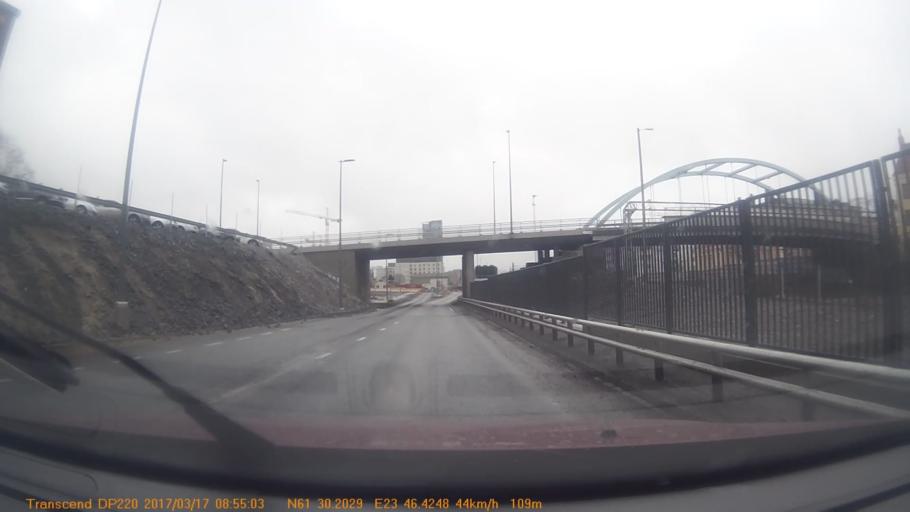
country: FI
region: Pirkanmaa
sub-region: Tampere
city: Tampere
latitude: 61.5034
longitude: 23.7738
